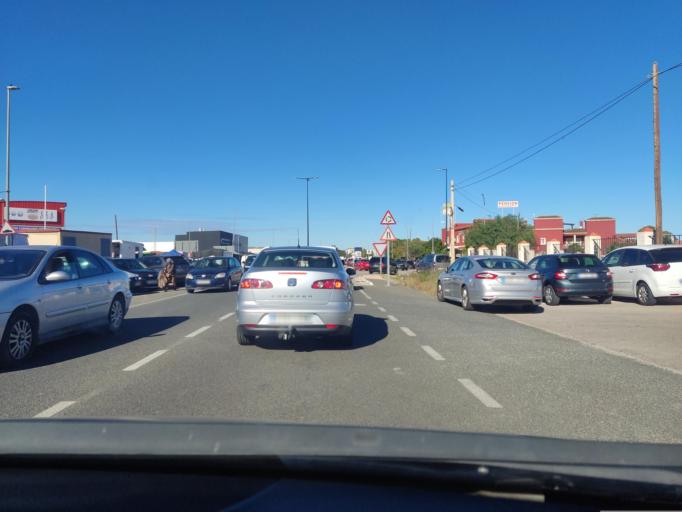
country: ES
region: Valencia
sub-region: Provincia de Alicante
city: Vergel
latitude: 38.8574
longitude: -0.0023
